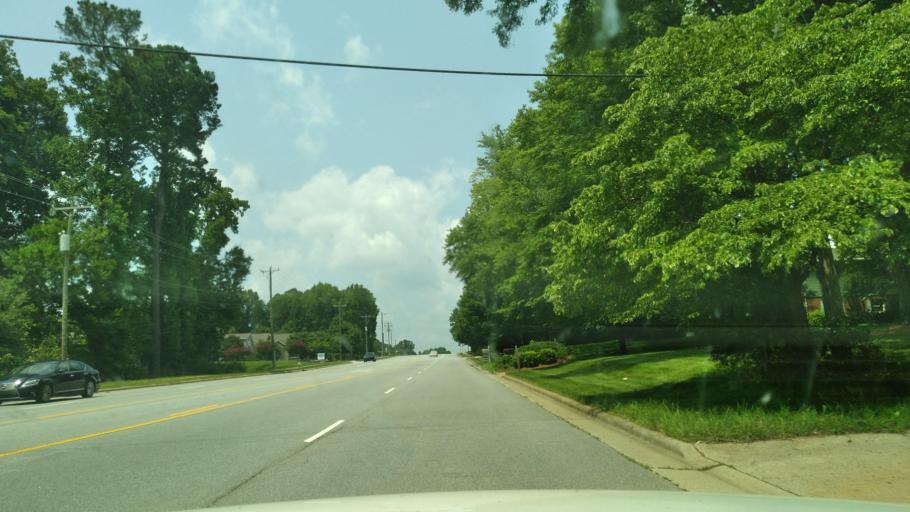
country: US
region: North Carolina
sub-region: Guilford County
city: Summerfield
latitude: 36.1200
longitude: -79.8917
